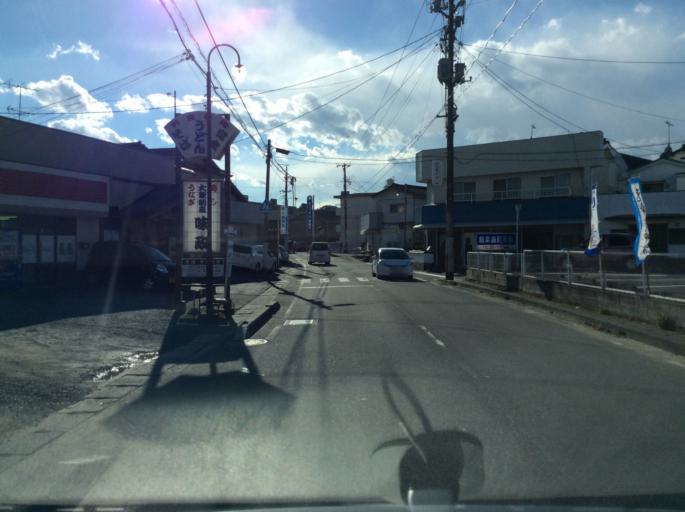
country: JP
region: Fukushima
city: Iwaki
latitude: 37.0646
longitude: 140.9374
